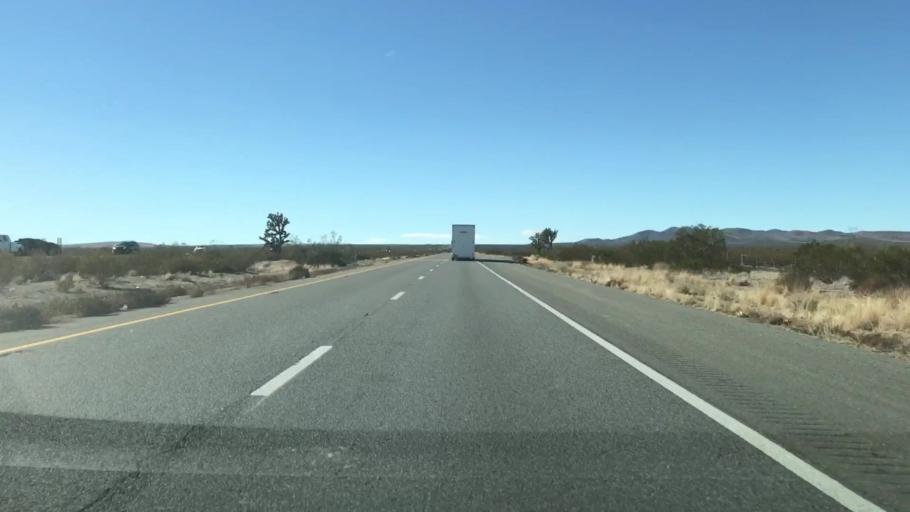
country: US
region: Nevada
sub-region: Clark County
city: Sandy Valley
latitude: 35.4277
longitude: -115.7213
